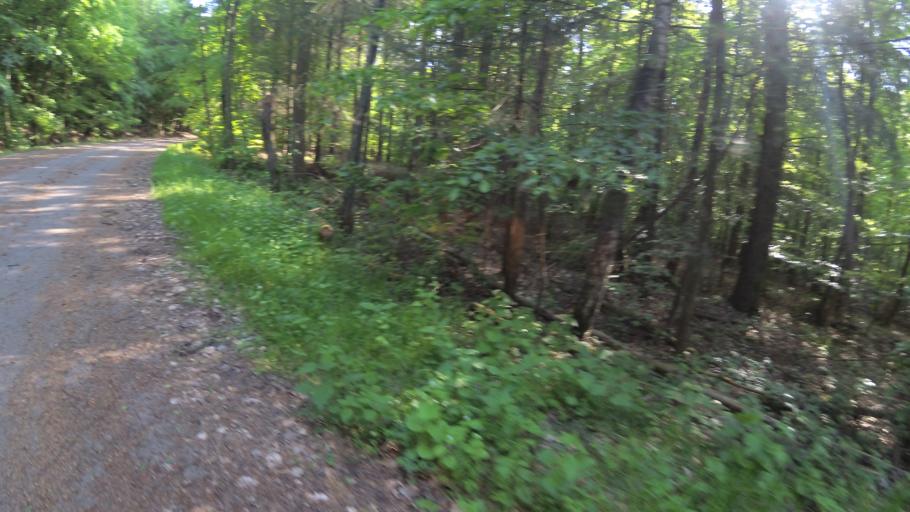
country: DE
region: Saarland
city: Marpingen
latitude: 49.4188
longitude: 7.0471
